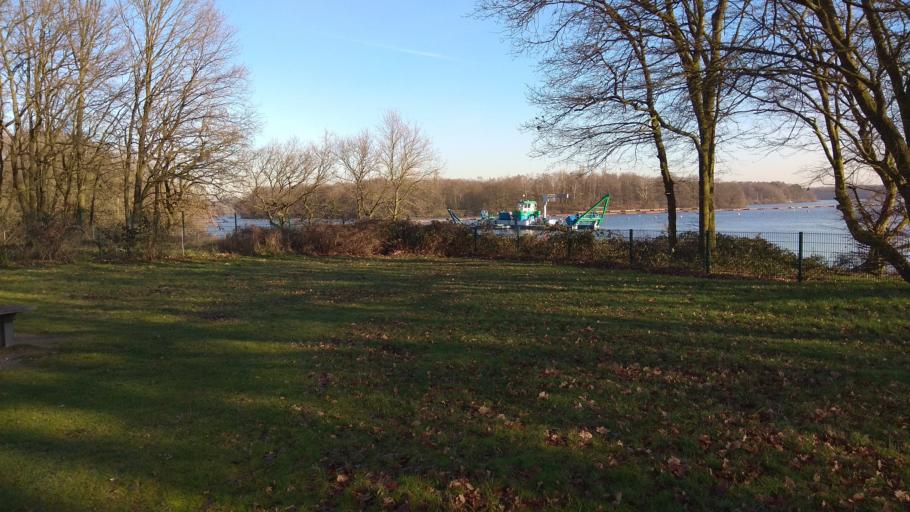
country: DE
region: North Rhine-Westphalia
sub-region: Regierungsbezirk Munster
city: Haltern
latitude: 51.7481
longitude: 7.2034
